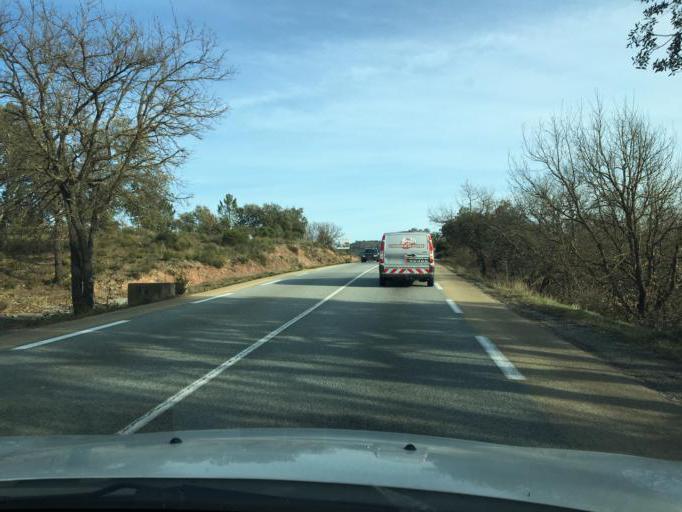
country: FR
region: Provence-Alpes-Cote d'Azur
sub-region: Departement du Var
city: Montauroux
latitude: 43.5485
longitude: 6.8034
